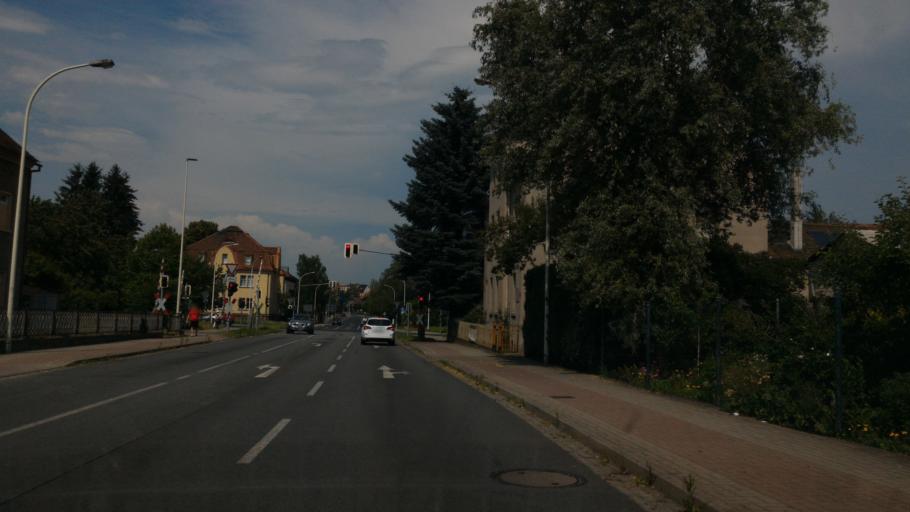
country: DE
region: Saxony
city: Zittau
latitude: 50.8880
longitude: 14.8026
